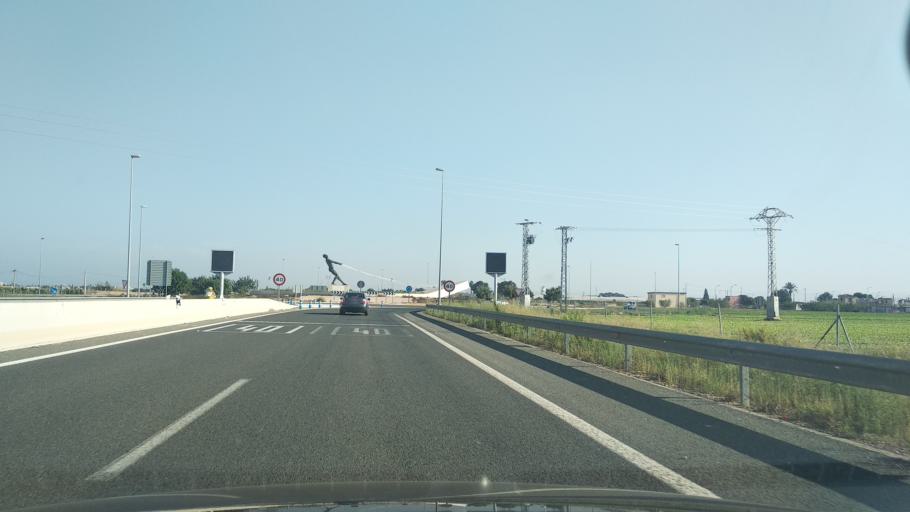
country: ES
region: Murcia
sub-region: Murcia
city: San Javier
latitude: 37.8224
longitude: -0.8504
